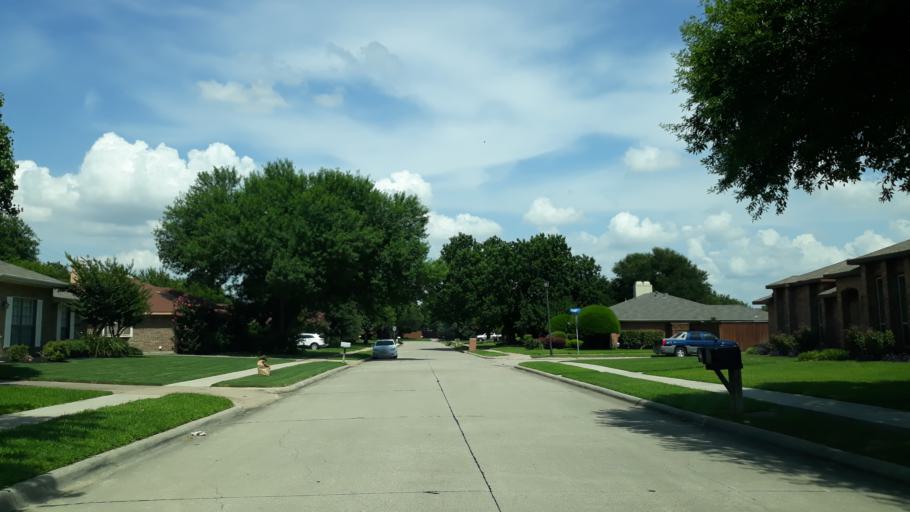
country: US
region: Texas
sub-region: Dallas County
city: Coppell
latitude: 32.9596
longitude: -97.0021
